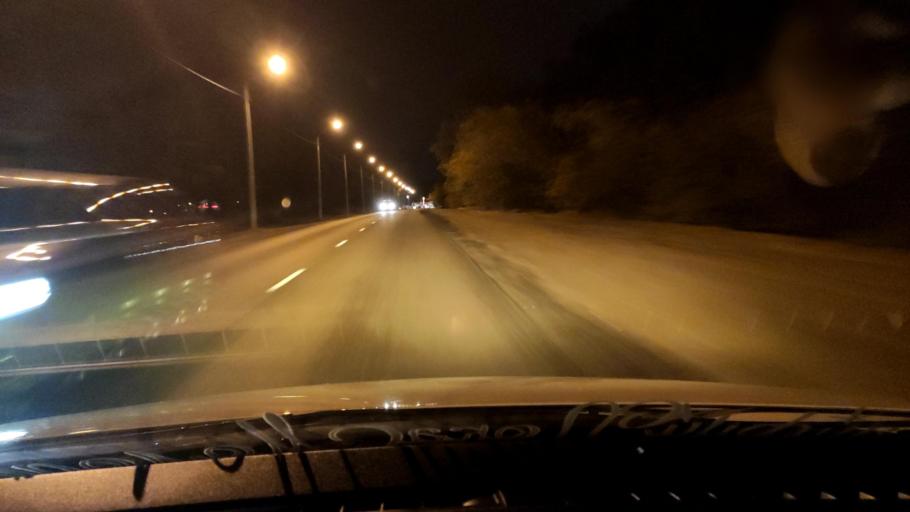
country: RU
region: Voronezj
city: Pridonskoy
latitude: 51.6923
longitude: 39.0842
